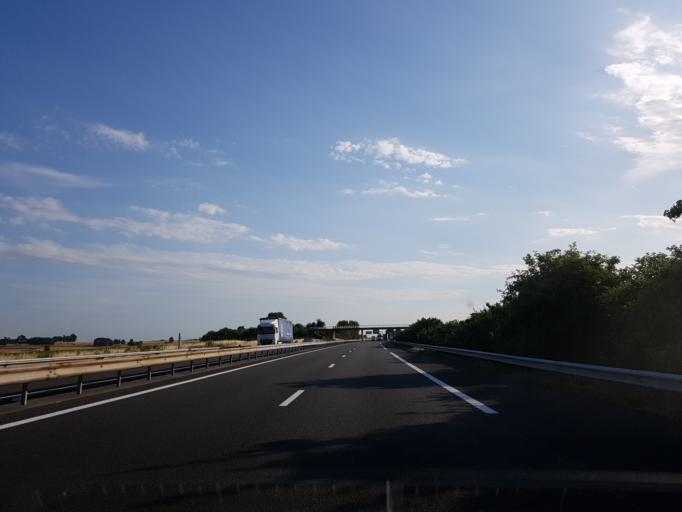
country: FR
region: Nord-Pas-de-Calais
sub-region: Departement du Pas-de-Calais
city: Bourlon
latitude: 50.1363
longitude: 3.1153
